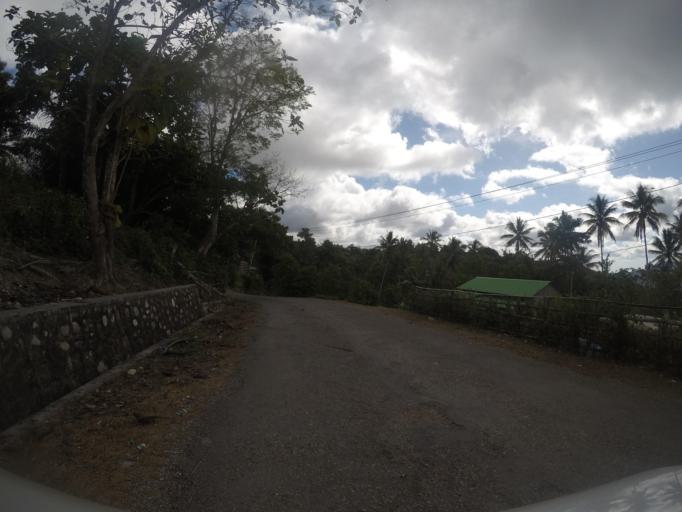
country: TL
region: Lautem
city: Lospalos
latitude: -8.5336
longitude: 126.9183
